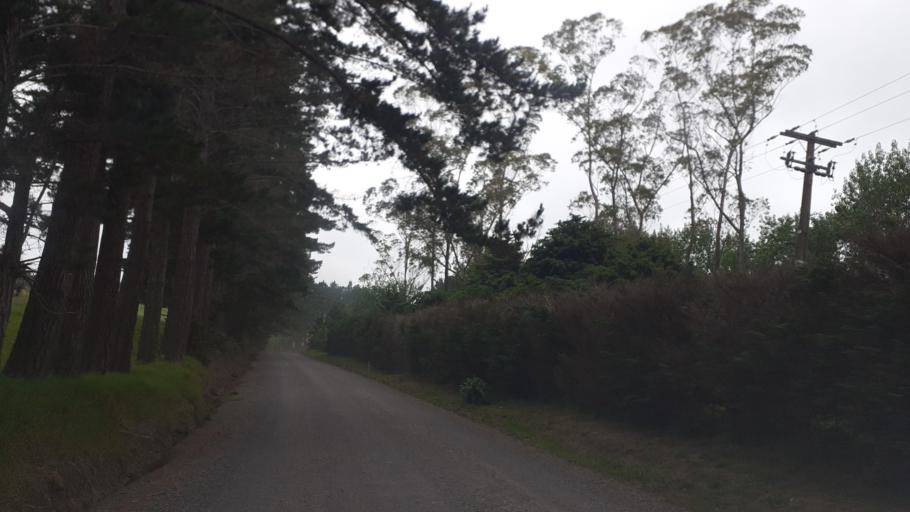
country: NZ
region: Northland
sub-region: Far North District
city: Kerikeri
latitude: -35.2814
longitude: 173.9597
